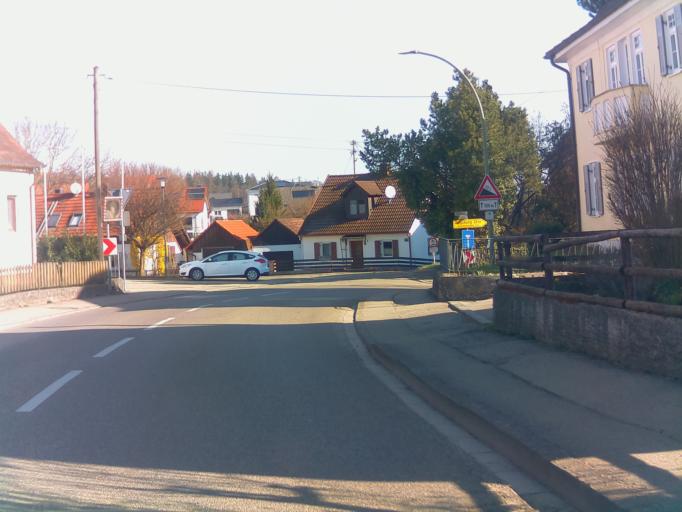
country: DE
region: Bavaria
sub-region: Swabia
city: Fischach
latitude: 48.2775
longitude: 10.7034
